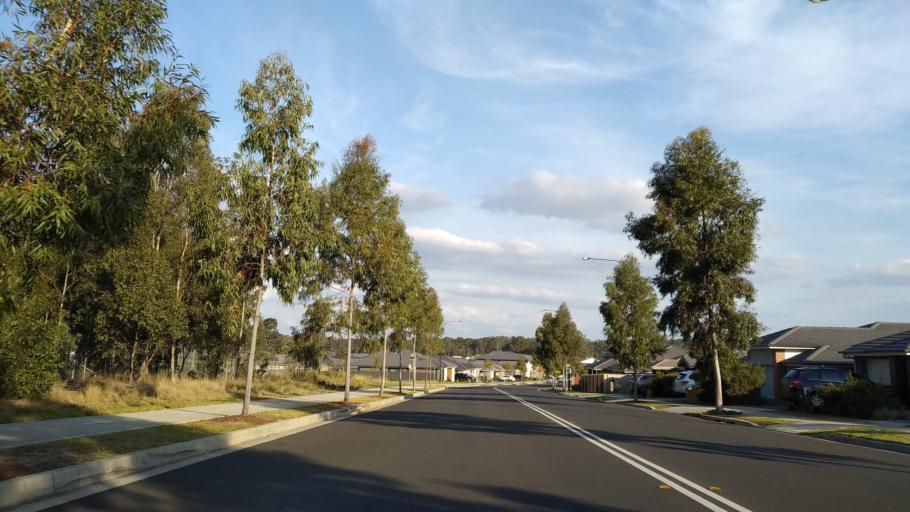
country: AU
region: New South Wales
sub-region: Penrith Municipality
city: Werrington Downs
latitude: -33.7237
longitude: 150.7357
